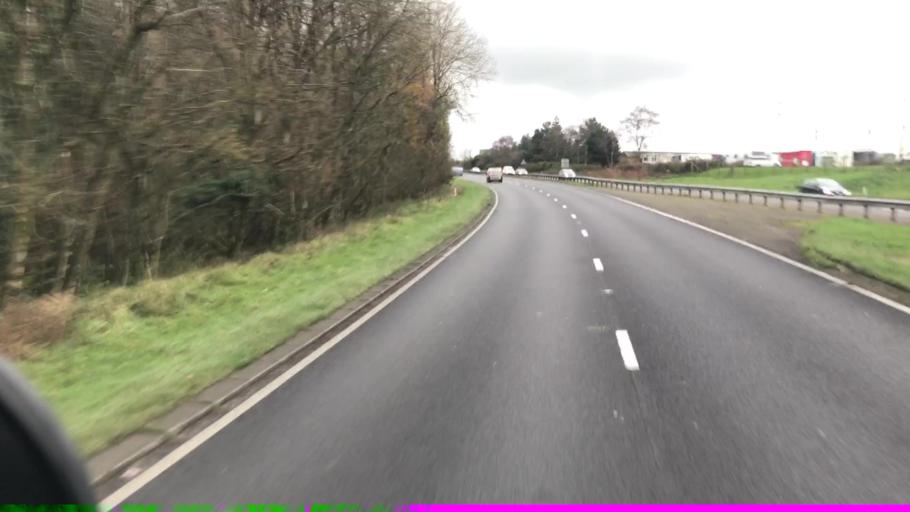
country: GB
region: England
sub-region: Devon
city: Chudleigh
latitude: 50.6376
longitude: -3.5638
